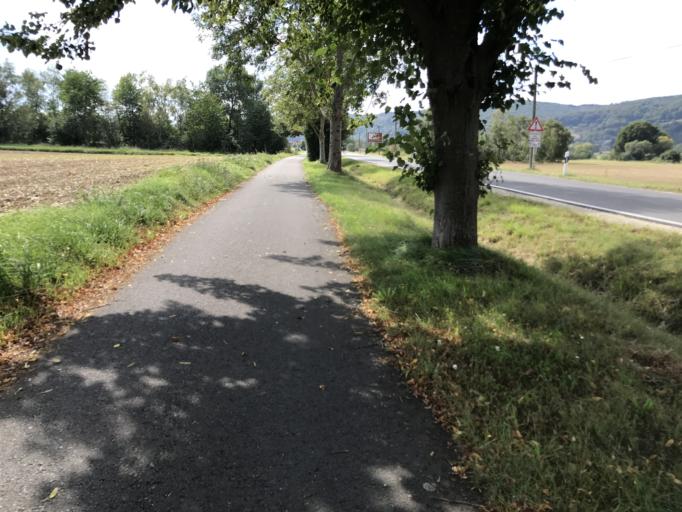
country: DE
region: Hesse
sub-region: Regierungsbezirk Kassel
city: Bad Sooden-Allendorf
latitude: 51.2862
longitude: 9.9762
